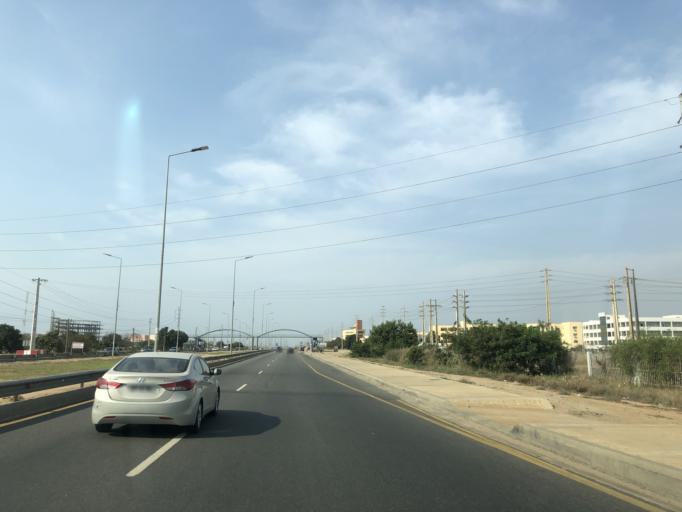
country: AO
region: Luanda
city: Luanda
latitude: -8.9696
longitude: 13.2556
